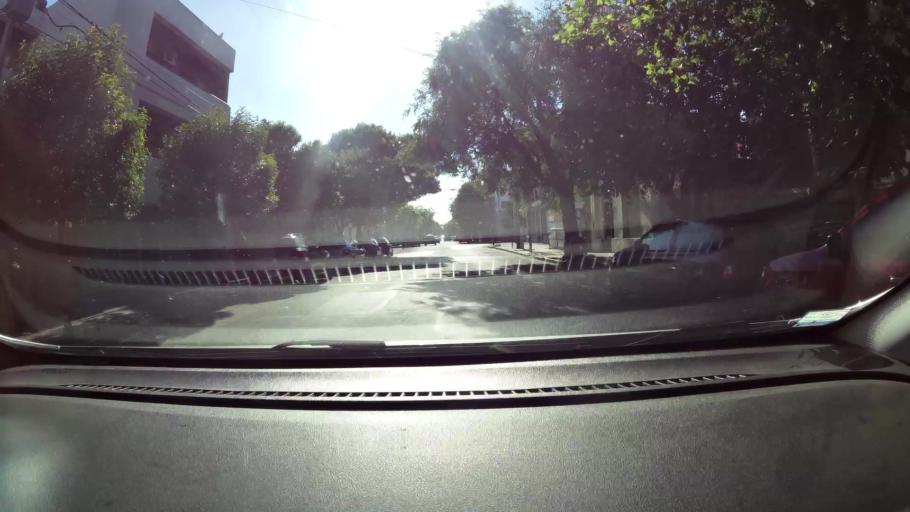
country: AR
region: Cordoba
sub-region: Departamento de Capital
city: Cordoba
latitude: -31.4255
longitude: -64.1489
